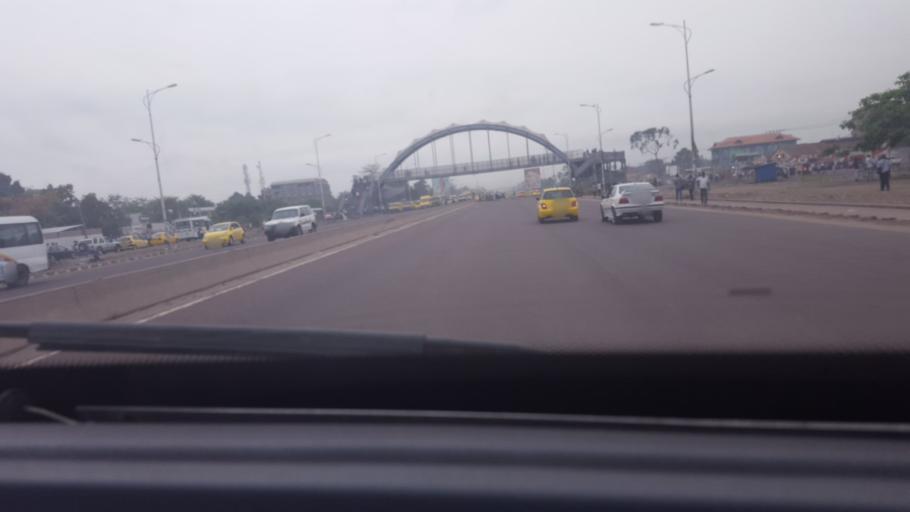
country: CD
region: Kinshasa
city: Kinshasa
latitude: -4.3631
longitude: 15.3405
